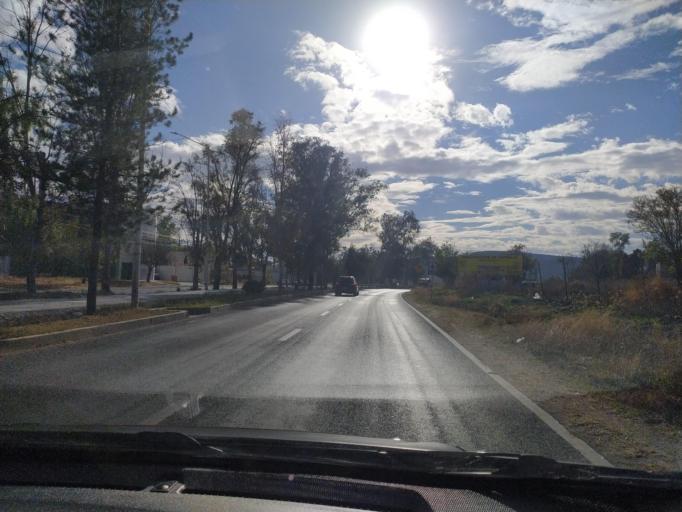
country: LA
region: Oudomxai
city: Muang La
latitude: 21.0295
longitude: 101.8458
